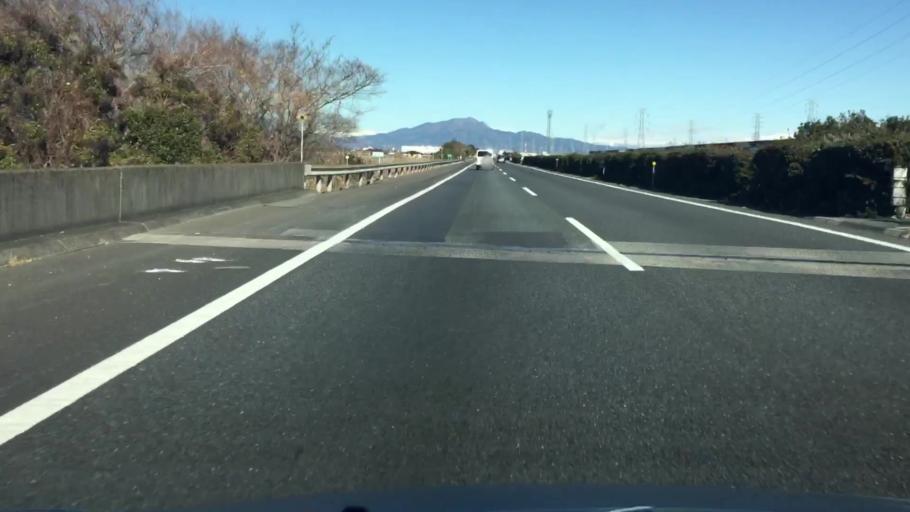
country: JP
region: Gunma
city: Maebashi-shi
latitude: 36.3899
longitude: 139.0258
